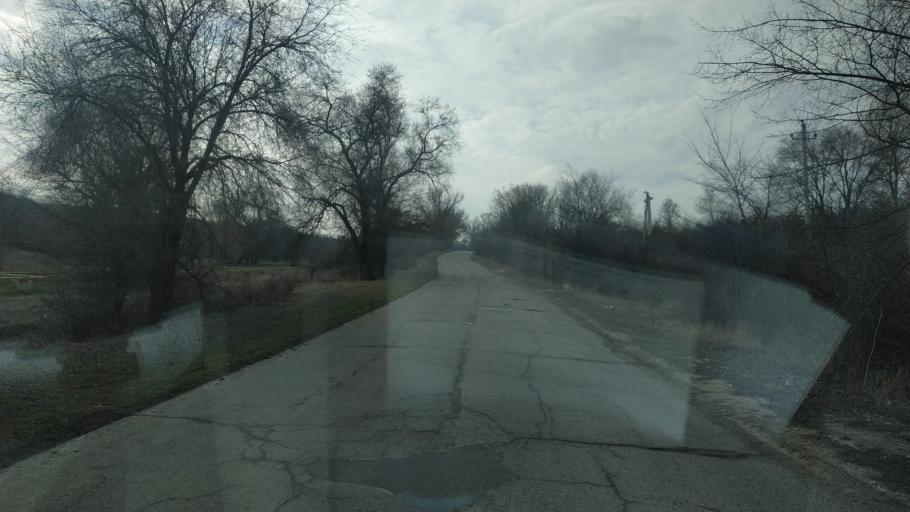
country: MD
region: Chisinau
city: Vadul lui Voda
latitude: 47.0040
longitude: 29.1120
